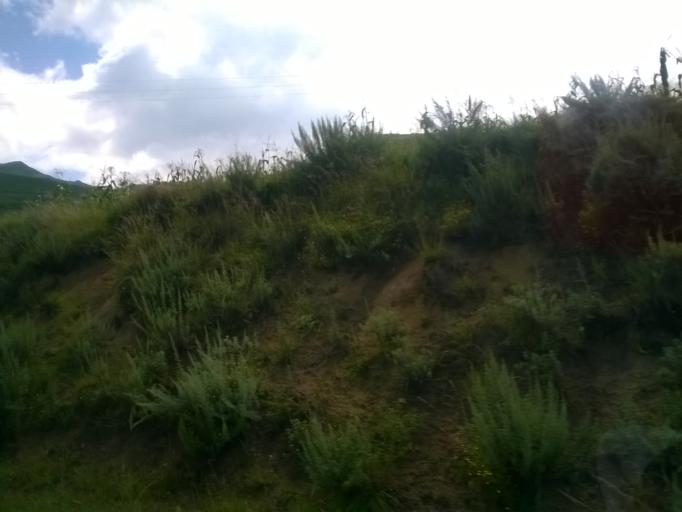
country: LS
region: Thaba-Tseka
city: Thaba-Tseka
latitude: -29.1225
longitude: 28.4918
